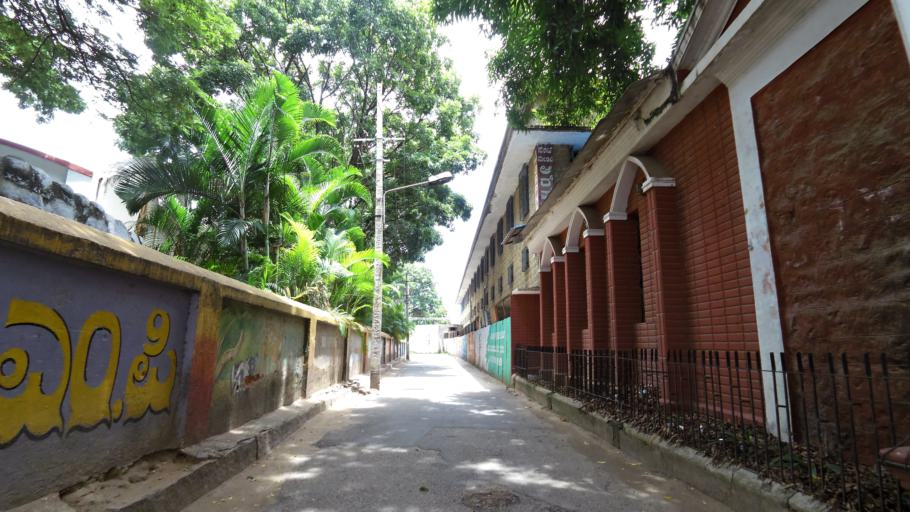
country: IN
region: Karnataka
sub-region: Bangalore Urban
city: Bangalore
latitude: 13.0022
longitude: 77.6258
